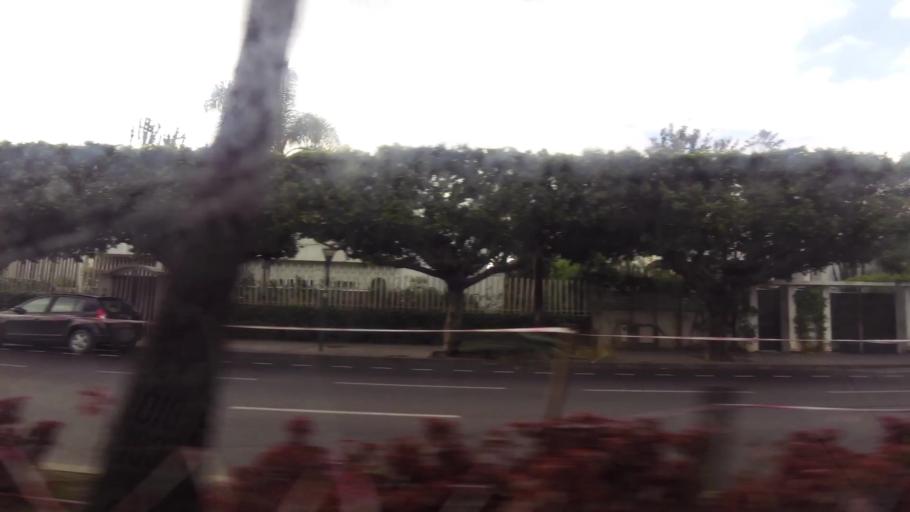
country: MA
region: Grand Casablanca
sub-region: Casablanca
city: Casablanca
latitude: 33.5868
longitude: -7.6501
